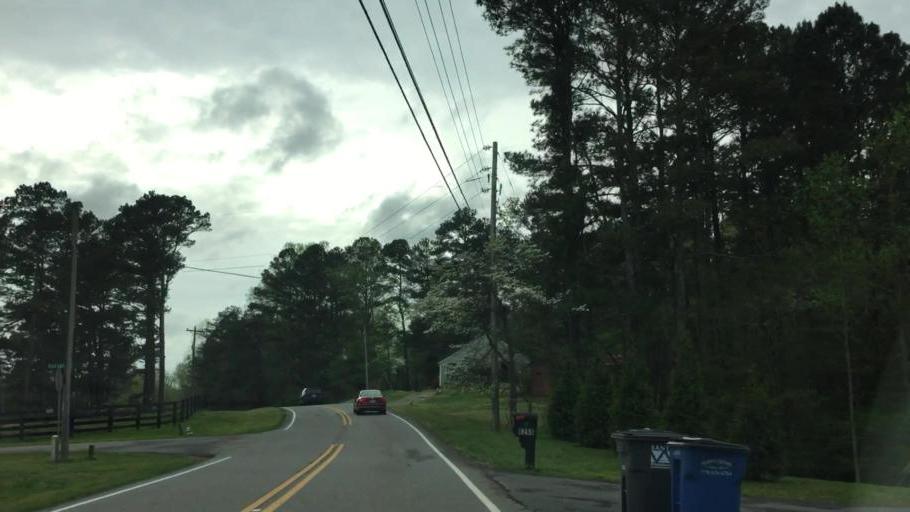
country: US
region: Georgia
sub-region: Fulton County
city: Milton
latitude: 34.2000
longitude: -84.3819
